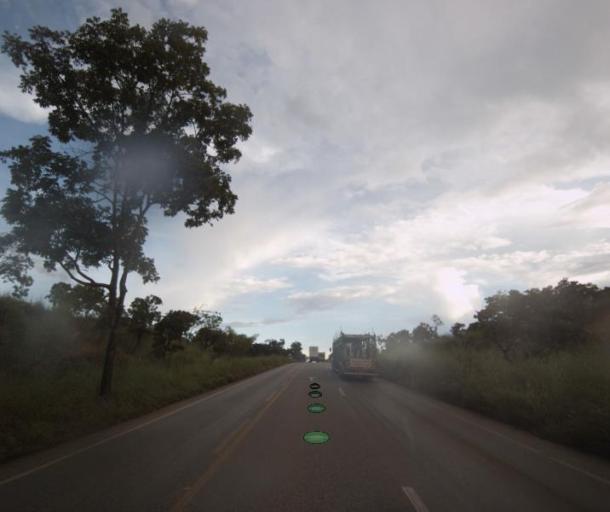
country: BR
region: Goias
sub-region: Porangatu
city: Porangatu
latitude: -13.9794
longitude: -49.0905
